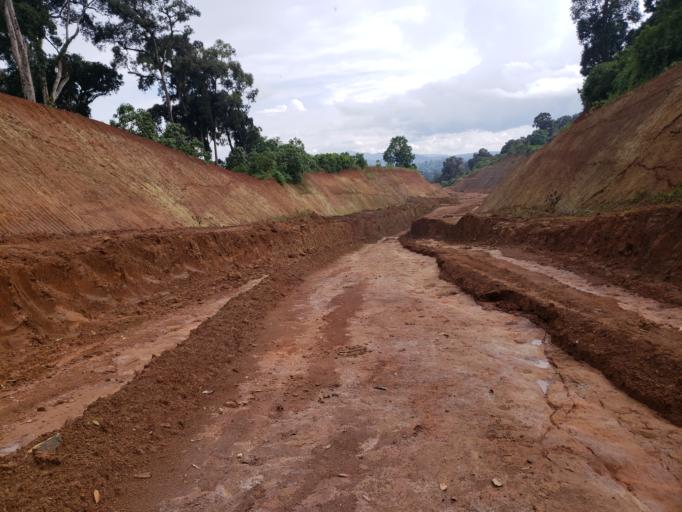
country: ET
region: Oromiya
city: Dodola
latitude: 6.5495
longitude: 39.4225
